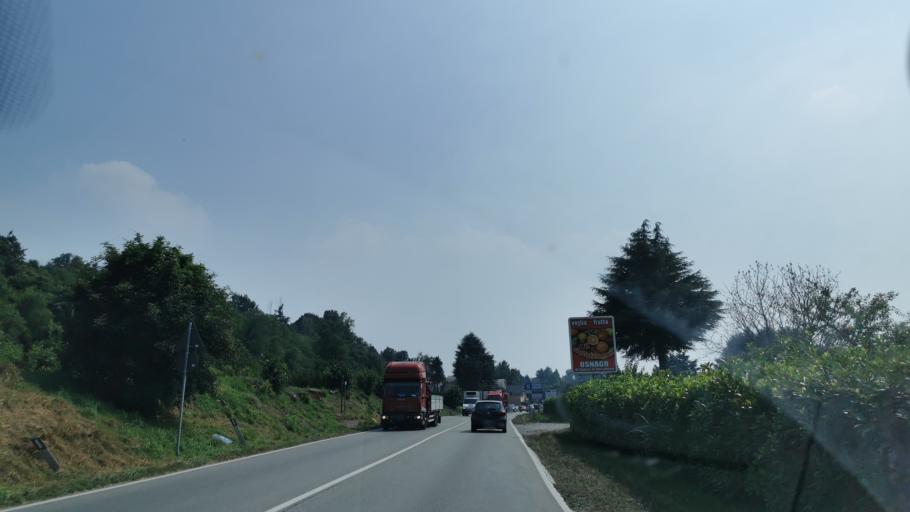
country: IT
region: Lombardy
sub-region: Provincia di Lecco
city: Canova-San Zeno
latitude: 45.7160
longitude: 9.4078
